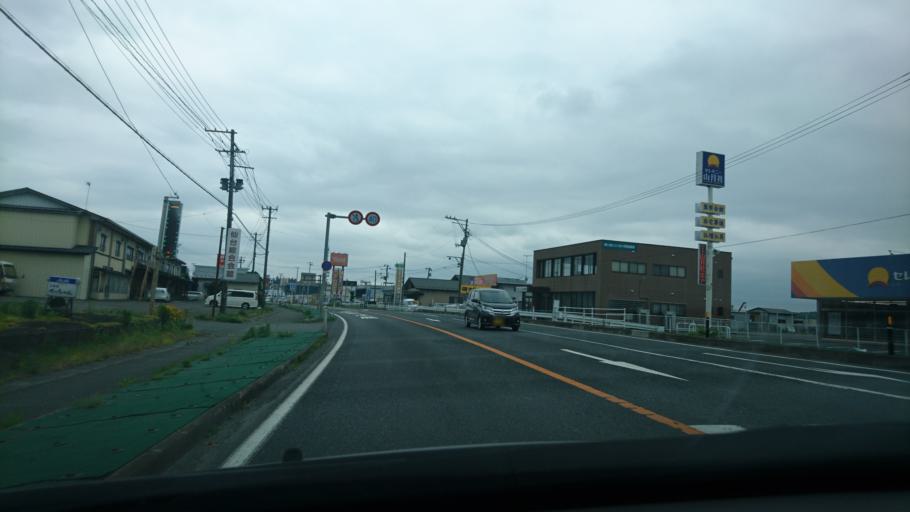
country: JP
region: Miyagi
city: Furukawa
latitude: 38.7485
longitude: 141.0143
